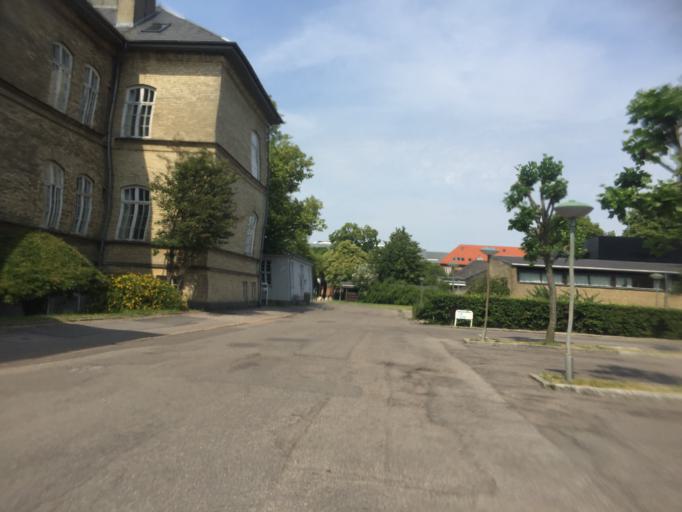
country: DK
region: Capital Region
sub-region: Frederiksberg Kommune
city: Frederiksberg
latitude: 55.6866
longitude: 12.5221
